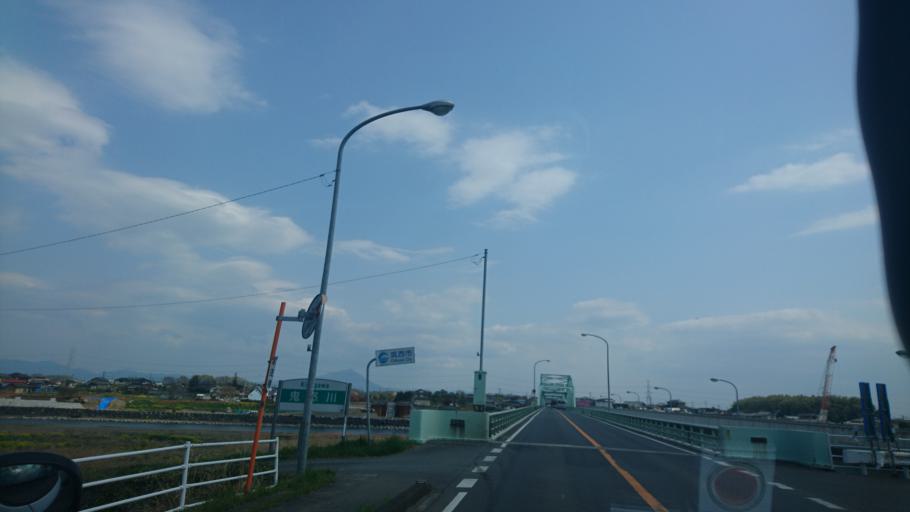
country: JP
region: Ibaraki
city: Yuki
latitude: 36.2782
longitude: 139.9043
